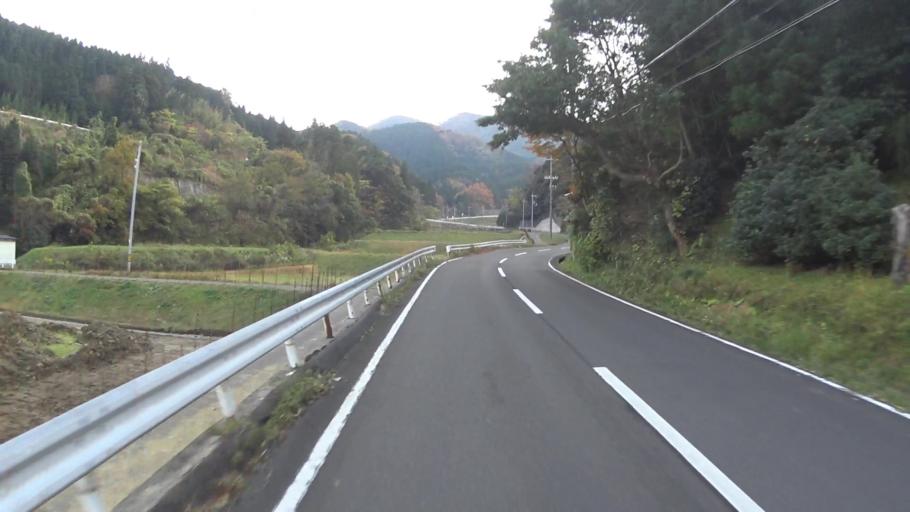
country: JP
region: Kyoto
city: Maizuru
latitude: 35.5627
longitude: 135.4540
